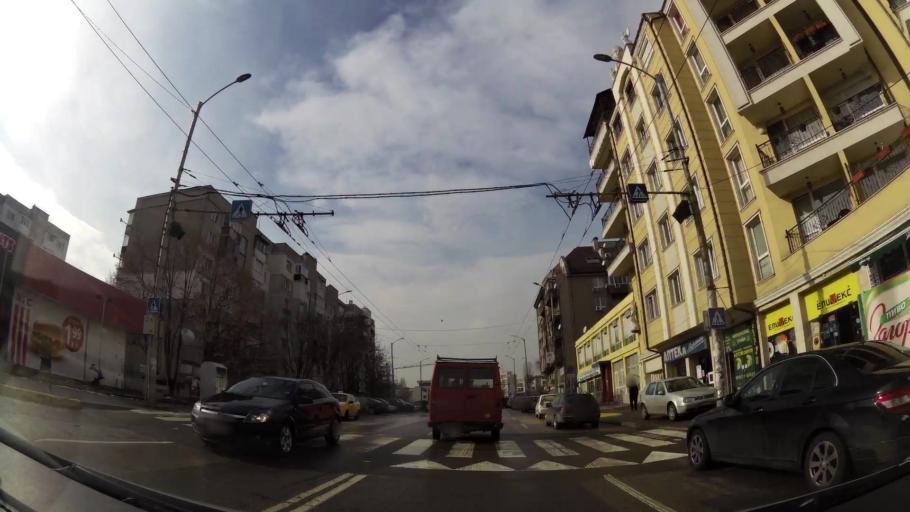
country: BG
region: Sofia-Capital
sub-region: Stolichna Obshtina
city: Sofia
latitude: 42.7149
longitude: 23.2598
